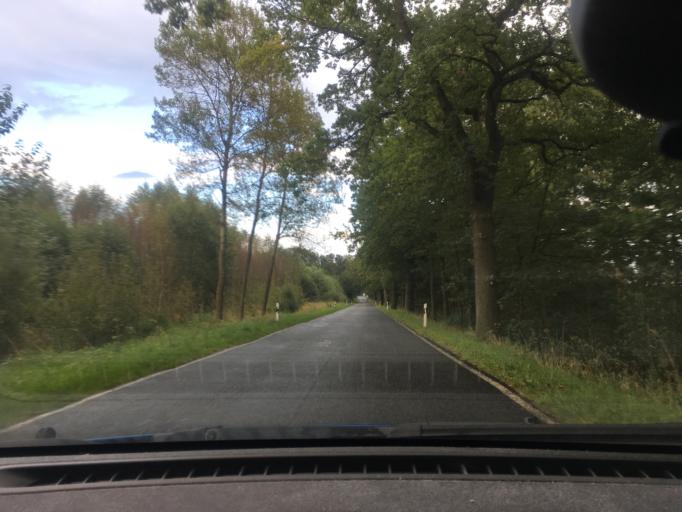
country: DE
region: Lower Saxony
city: Neu Darchau
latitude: 53.3320
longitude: 10.8727
